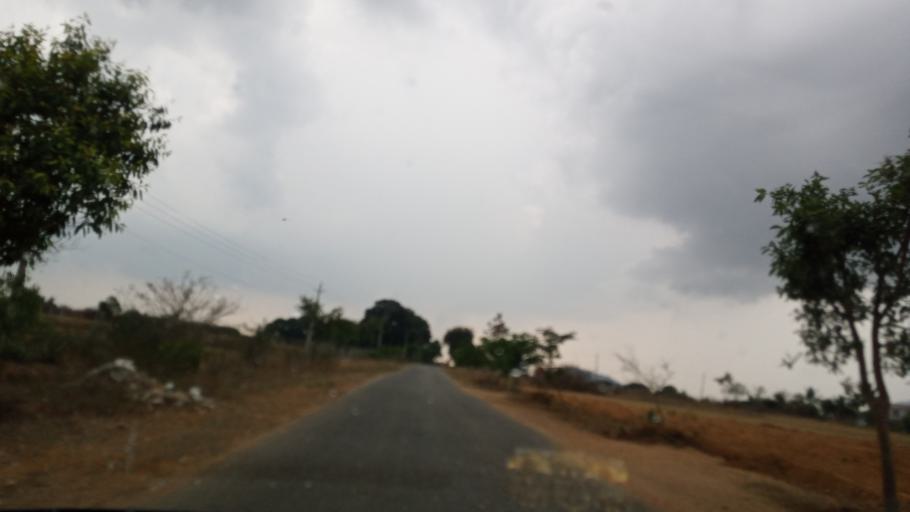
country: IN
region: Karnataka
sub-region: Kolar
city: Mulbagal
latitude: 13.1368
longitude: 78.3603
